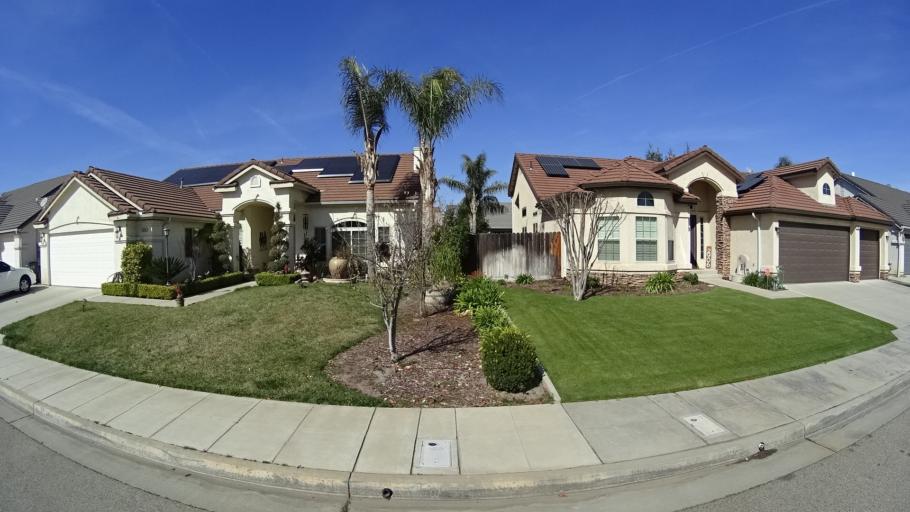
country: US
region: California
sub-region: Fresno County
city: Clovis
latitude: 36.8478
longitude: -119.7319
